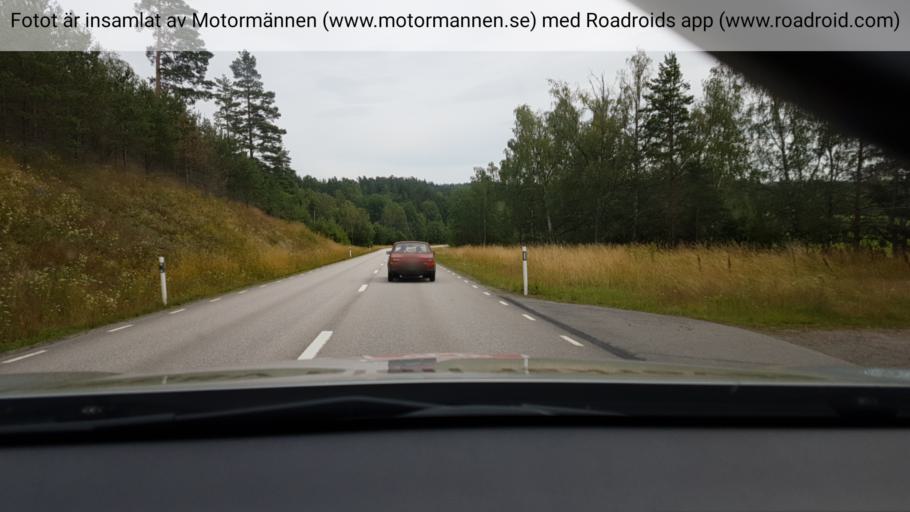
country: SE
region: Vaestra Goetaland
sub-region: Bengtsfors Kommun
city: Billingsfors
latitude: 58.9219
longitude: 12.2193
